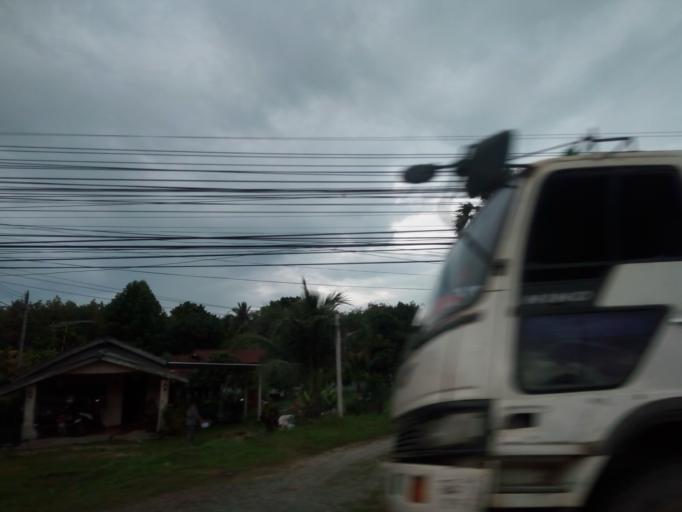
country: TH
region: Phuket
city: Thalang
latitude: 8.0714
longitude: 98.3895
